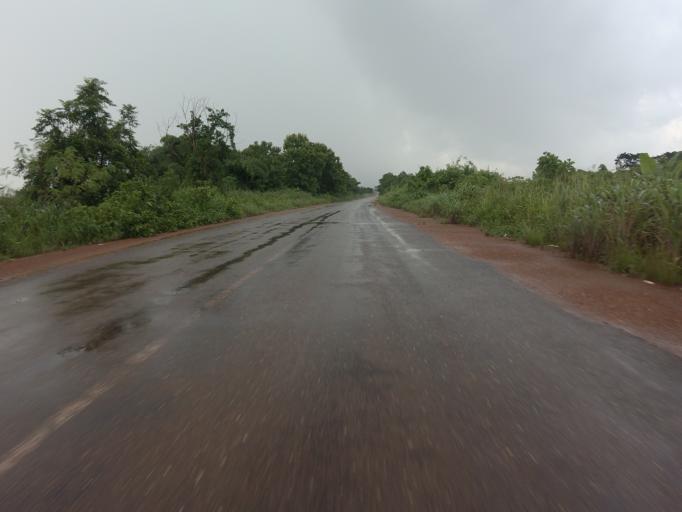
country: GH
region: Volta
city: Hohoe
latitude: 7.0571
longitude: 0.4282
